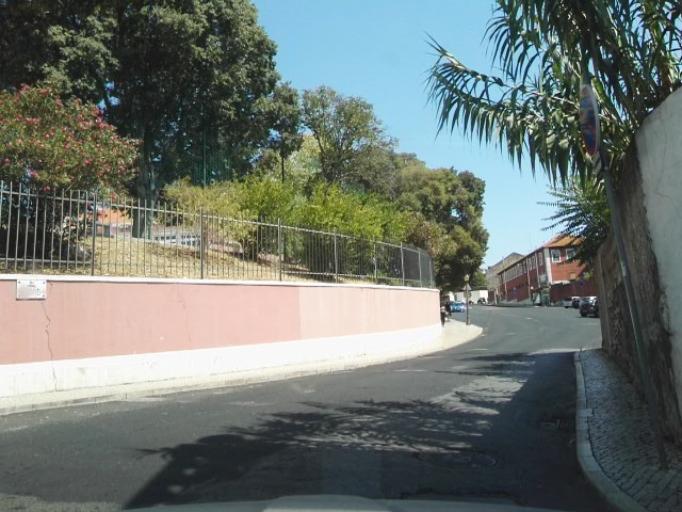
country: PT
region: Setubal
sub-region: Almada
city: Cacilhas
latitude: 38.7126
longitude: -9.1675
